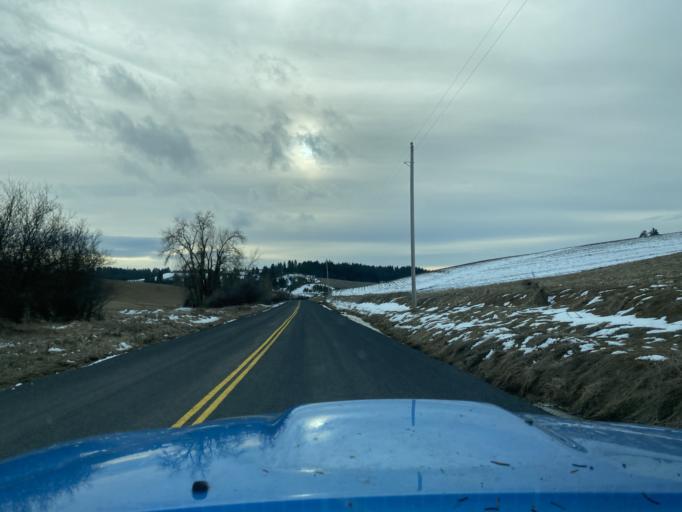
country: US
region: Idaho
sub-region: Latah County
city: Moscow
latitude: 46.6904
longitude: -116.8731
